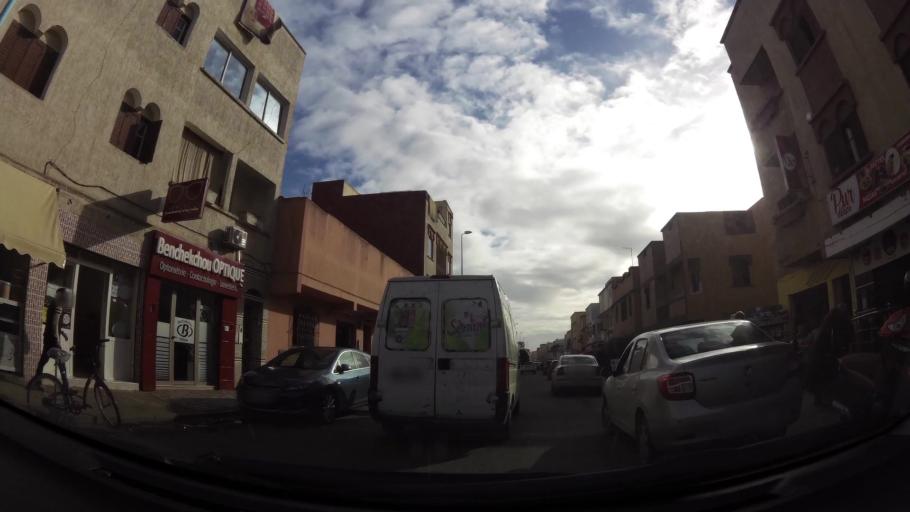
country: MA
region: Doukkala-Abda
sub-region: El-Jadida
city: El Jadida
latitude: 33.2433
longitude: -8.5259
